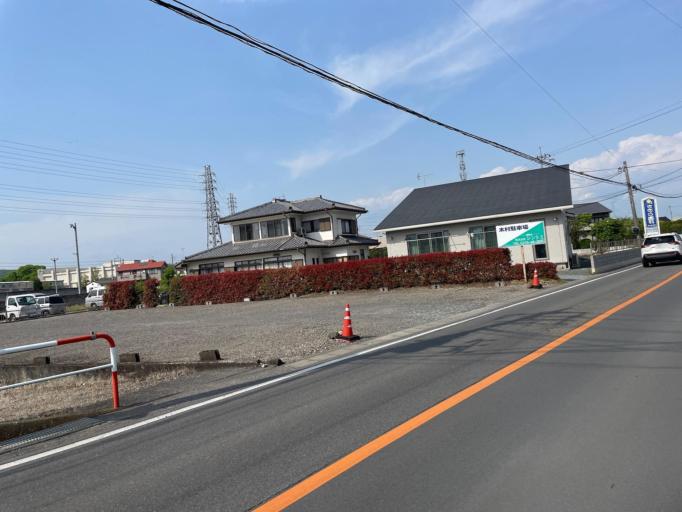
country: JP
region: Gunma
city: Ota
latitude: 36.2953
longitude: 139.3889
